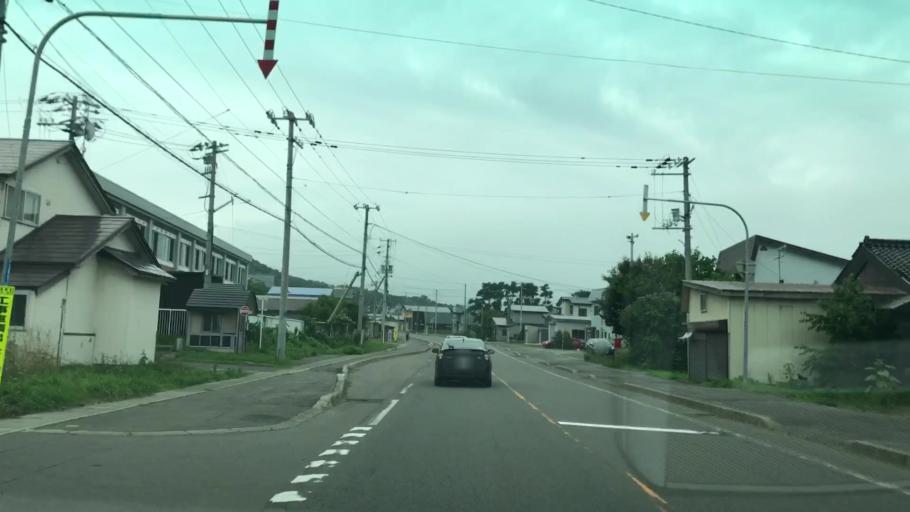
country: JP
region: Hokkaido
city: Iwanai
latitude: 42.7767
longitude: 140.3056
